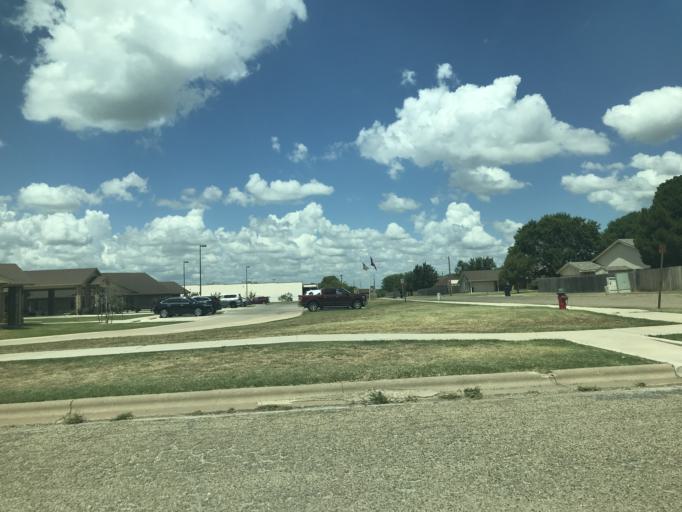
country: US
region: Texas
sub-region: Taylor County
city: Abilene
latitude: 32.4394
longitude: -99.7024
